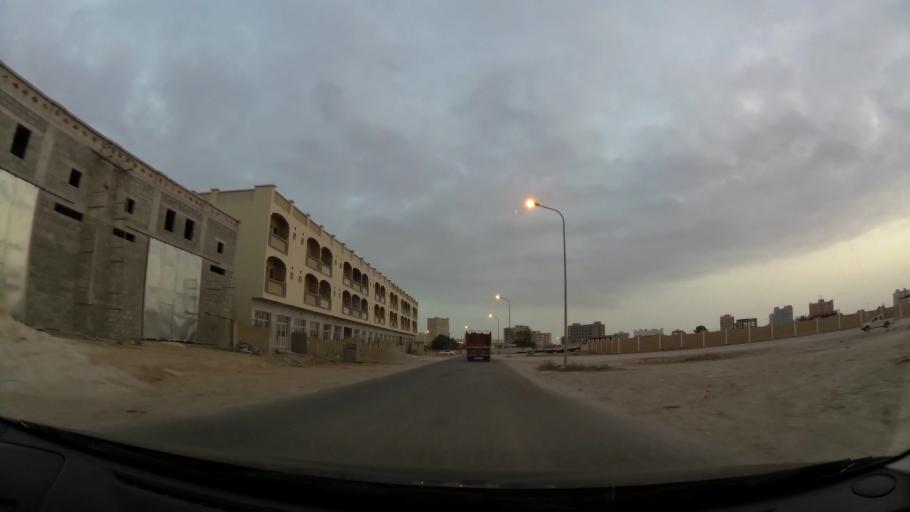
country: OM
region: Zufar
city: Salalah
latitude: 17.0299
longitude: 54.0335
